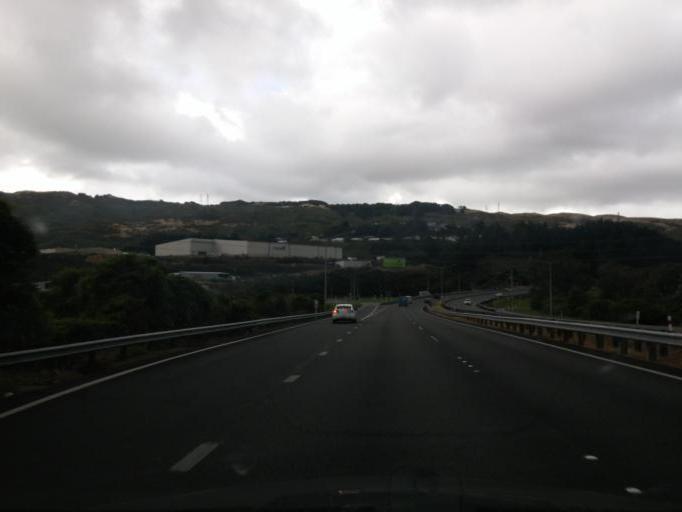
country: NZ
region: Wellington
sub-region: Porirua City
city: Porirua
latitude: -41.1830
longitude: 174.8305
